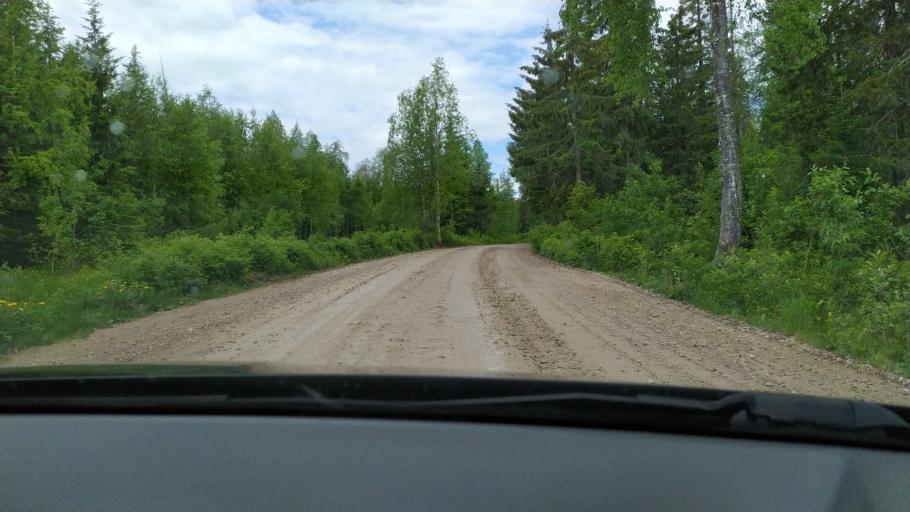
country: RU
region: Perm
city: Gremyachinsk
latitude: 58.5107
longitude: 57.8150
